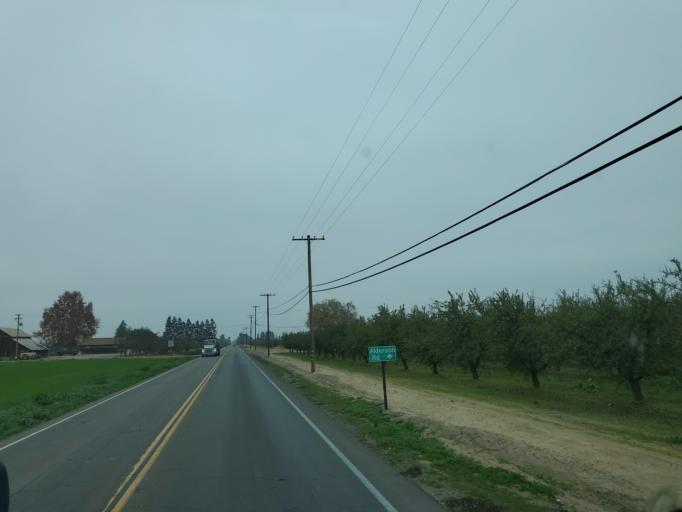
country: US
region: California
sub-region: Stanislaus County
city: Hughson
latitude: 37.5537
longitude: -120.8471
